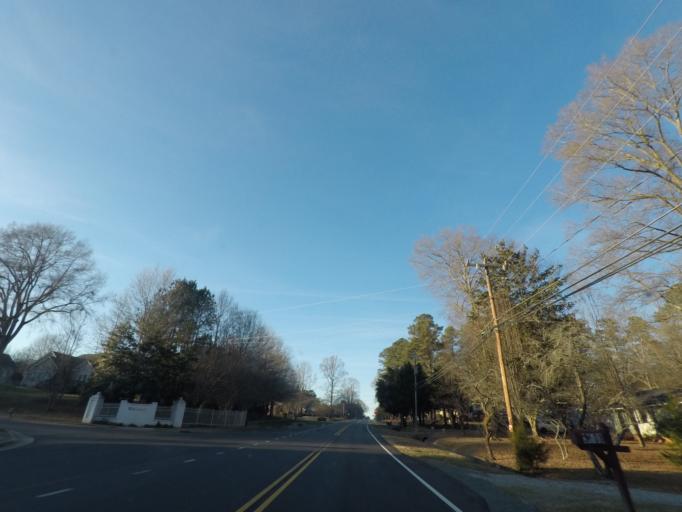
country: US
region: North Carolina
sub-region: Durham County
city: Durham
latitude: 36.0487
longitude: -78.9703
